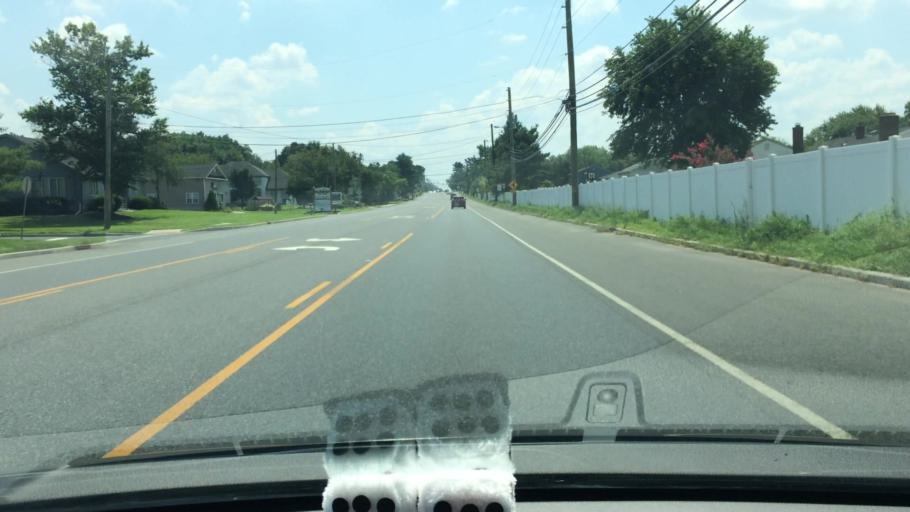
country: US
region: New Jersey
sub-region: Gloucester County
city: Turnersville
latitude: 39.7579
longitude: -75.0819
